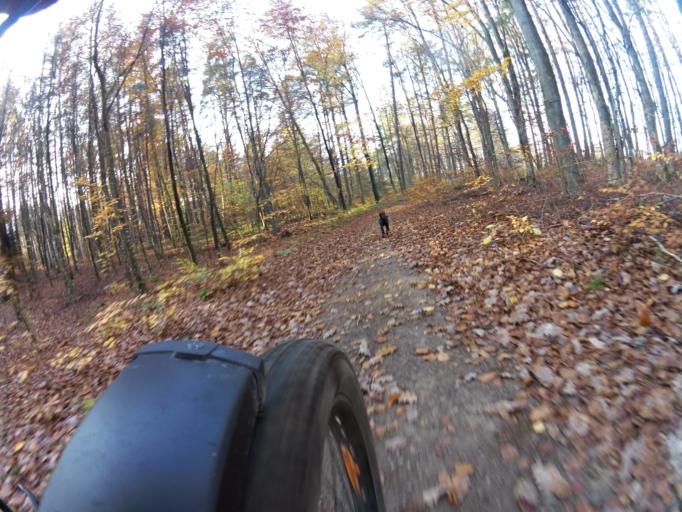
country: PL
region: Pomeranian Voivodeship
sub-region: Powiat pucki
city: Krokowa
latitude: 54.7295
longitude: 18.1997
